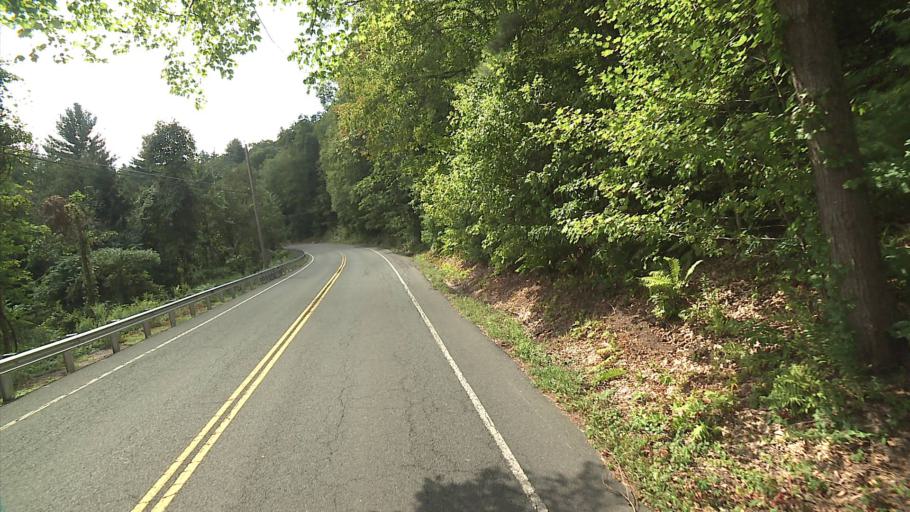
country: US
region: Massachusetts
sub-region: Hampden County
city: Granville
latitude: 42.0307
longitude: -72.8629
